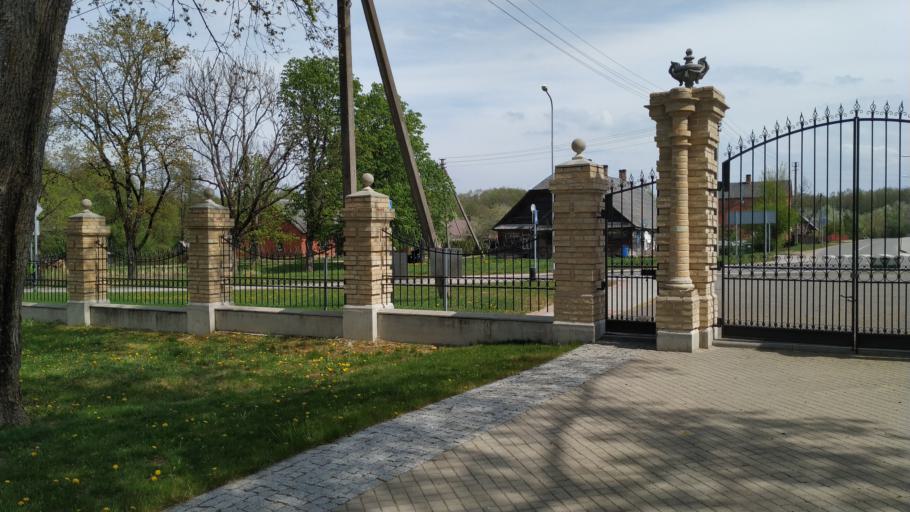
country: LT
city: Salcininkai
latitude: 54.4335
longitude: 25.2997
